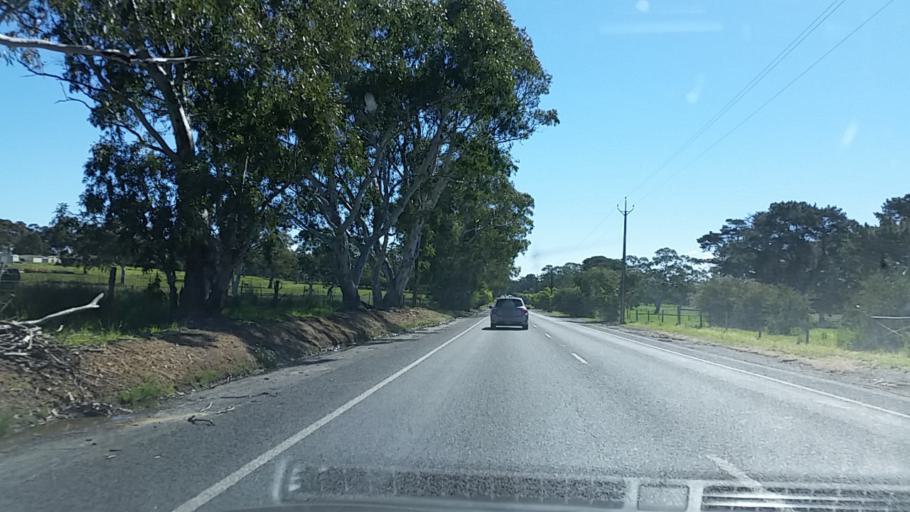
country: AU
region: South Australia
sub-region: Mount Barker
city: Meadows
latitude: -35.1825
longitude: 138.7497
